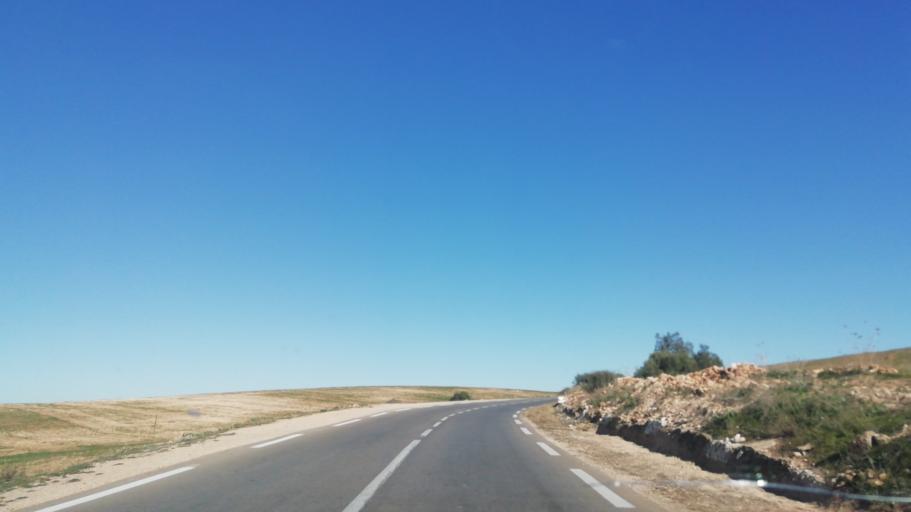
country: DZ
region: Tlemcen
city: Beni Mester
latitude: 34.8261
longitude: -1.6029
